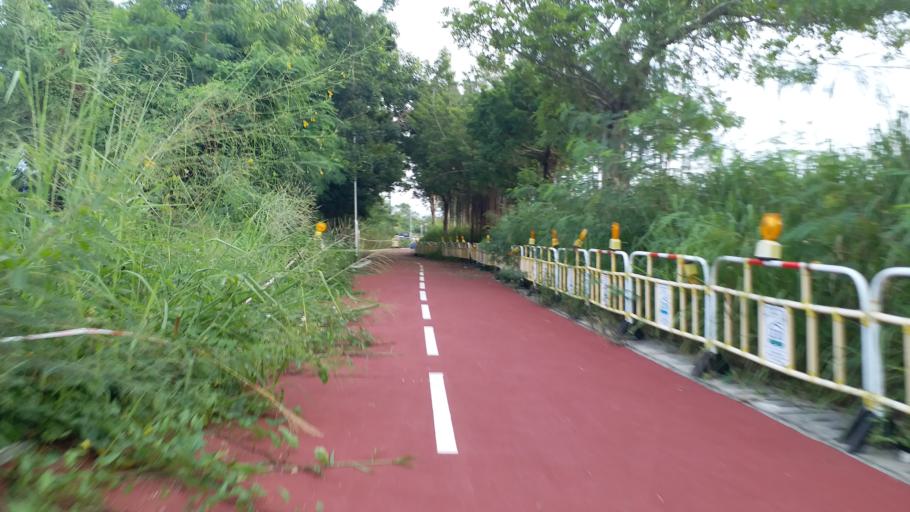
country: HK
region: Yuen Long
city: Yuen Long Kau Hui
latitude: 22.4626
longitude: 114.0458
